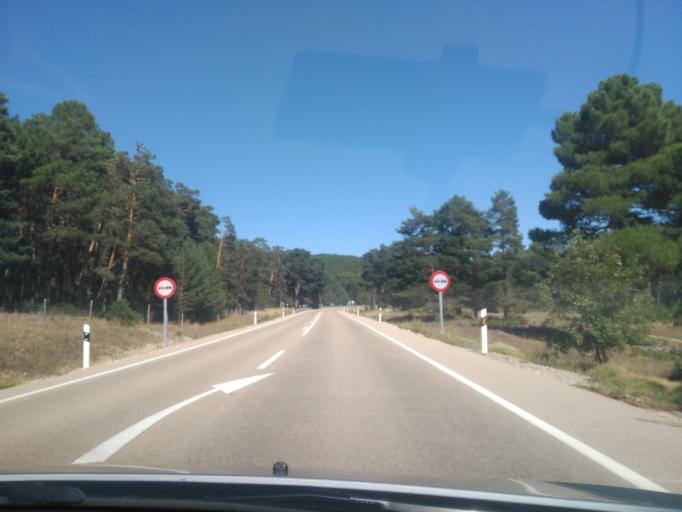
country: ES
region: Castille and Leon
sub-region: Provincia de Soria
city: Navaleno
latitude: 41.8382
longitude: -3.0313
